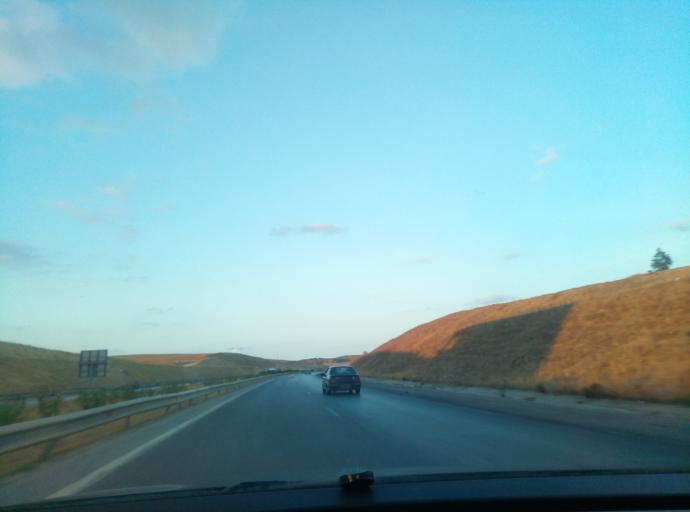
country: TN
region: Manouba
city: Manouba
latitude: 36.7512
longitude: 10.0404
